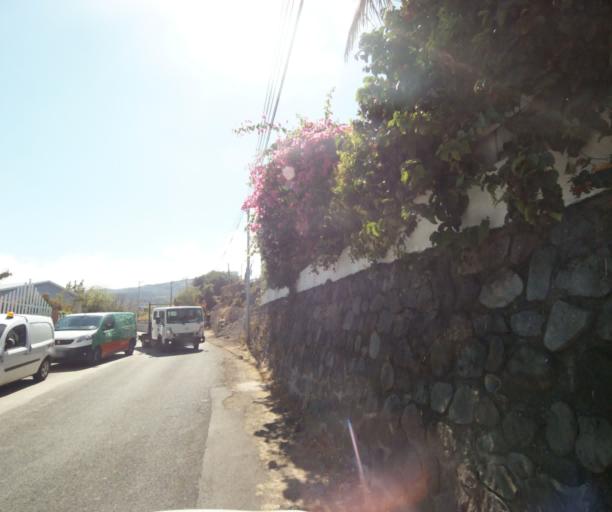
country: RE
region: Reunion
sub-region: Reunion
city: Saint-Paul
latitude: -20.9876
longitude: 55.3240
